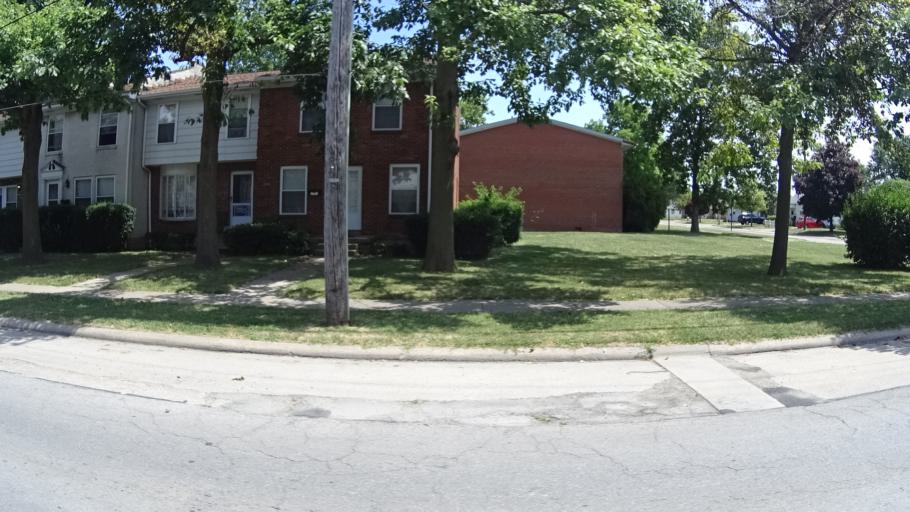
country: US
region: Ohio
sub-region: Erie County
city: Sandusky
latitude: 41.4370
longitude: -82.7199
